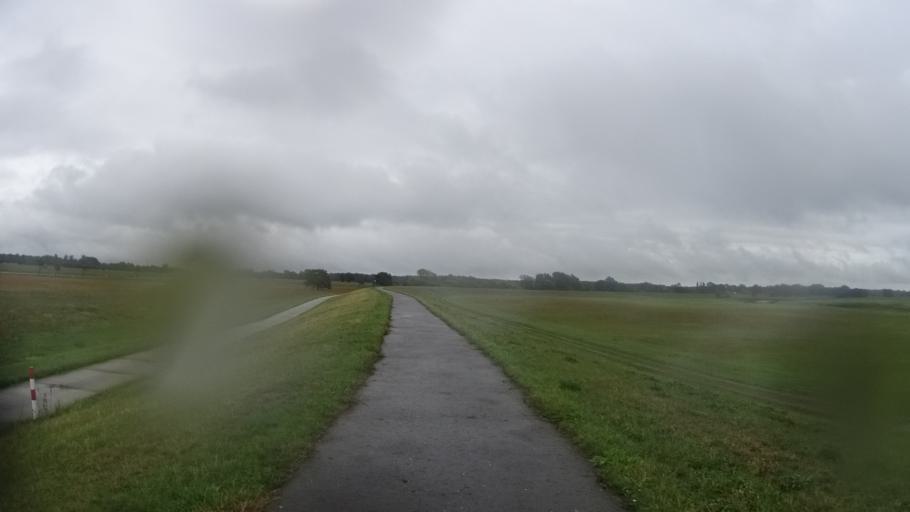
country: DE
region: Lower Saxony
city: Damnatz
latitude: 53.1764
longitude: 11.1509
